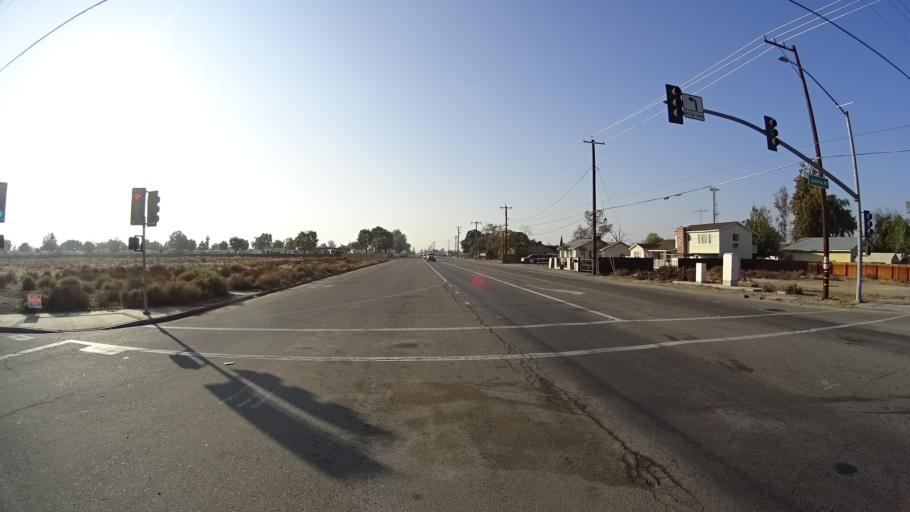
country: US
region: California
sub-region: Kern County
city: Rosedale
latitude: 35.3835
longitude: -119.1544
